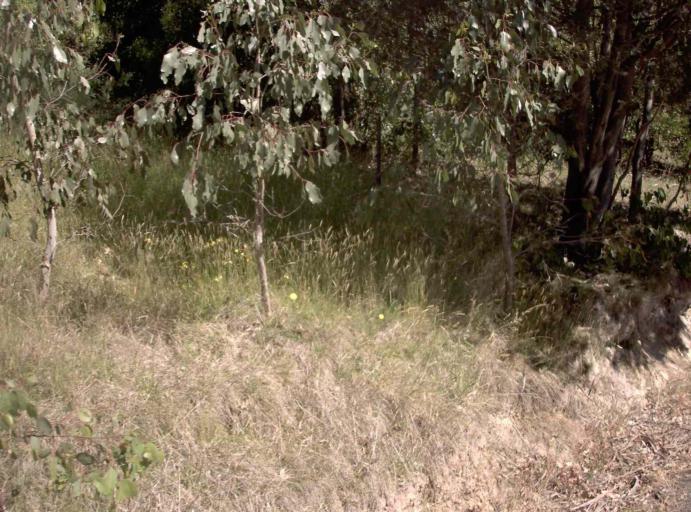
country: AU
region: New South Wales
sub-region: Bombala
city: Bombala
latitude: -37.0547
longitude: 148.8056
